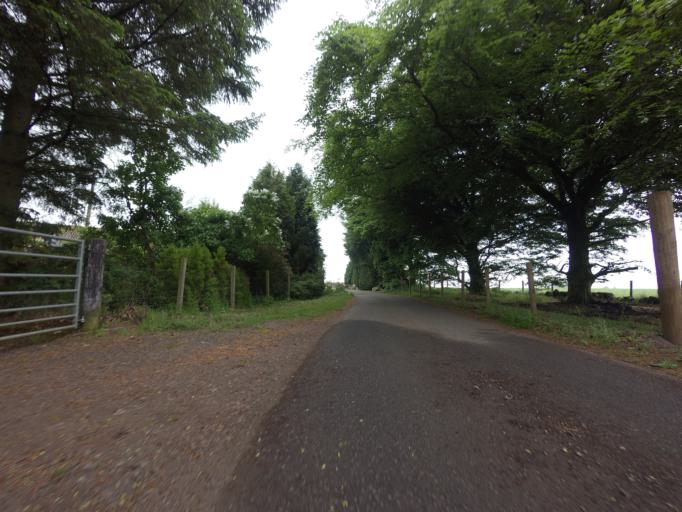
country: GB
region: Scotland
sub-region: Fife
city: Ballingry
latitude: 56.2379
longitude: -3.3439
